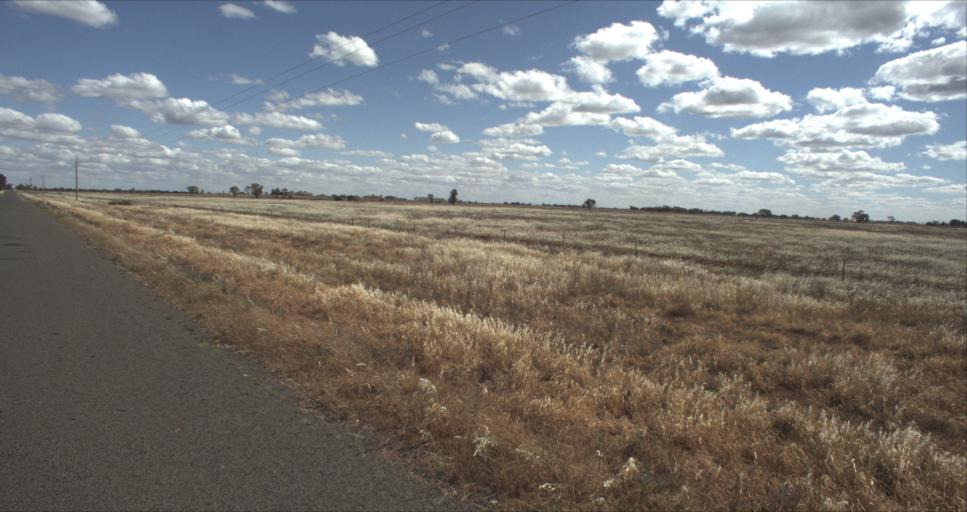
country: AU
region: New South Wales
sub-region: Leeton
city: Leeton
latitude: -34.4670
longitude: 146.2516
